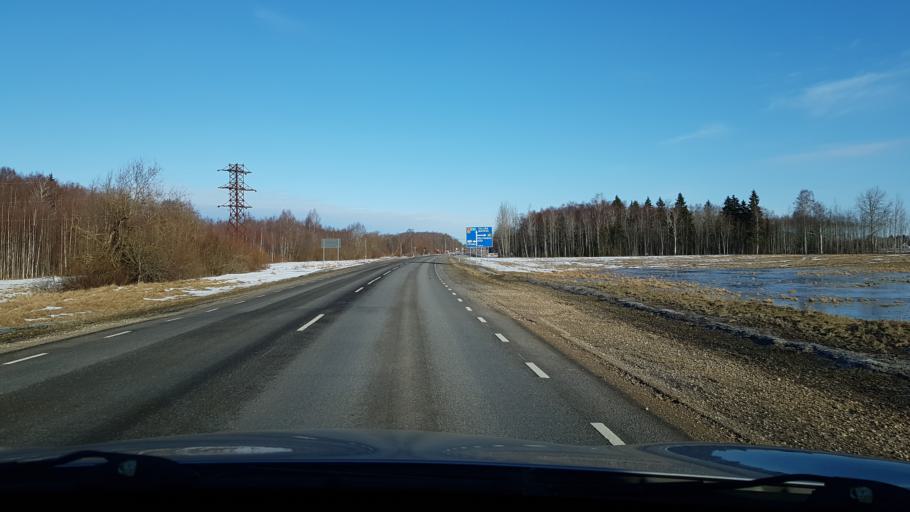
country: EE
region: Viljandimaa
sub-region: Vohma linn
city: Vohma
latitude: 58.6241
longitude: 25.5691
